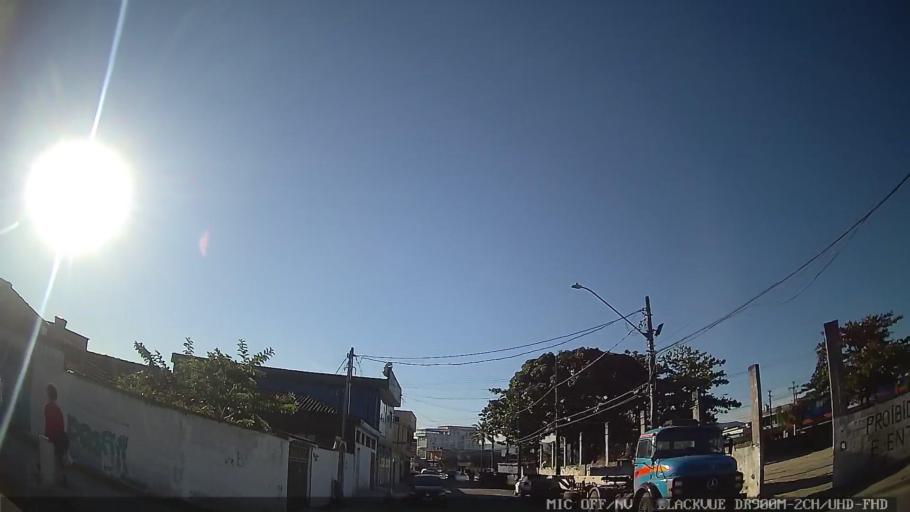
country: BR
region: Sao Paulo
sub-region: Santos
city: Santos
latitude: -23.9520
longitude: -46.2943
